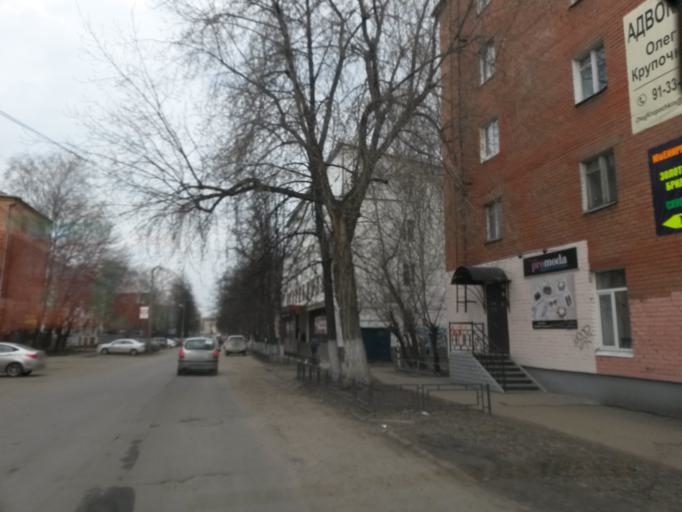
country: RU
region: Jaroslavl
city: Yaroslavl
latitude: 57.6282
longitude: 39.8580
